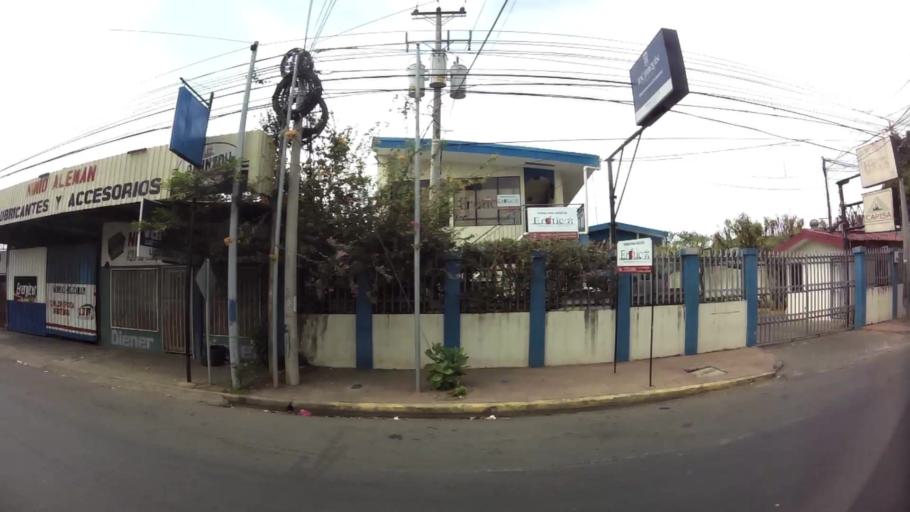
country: NI
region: Managua
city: Managua
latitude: 12.1452
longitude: -86.2768
